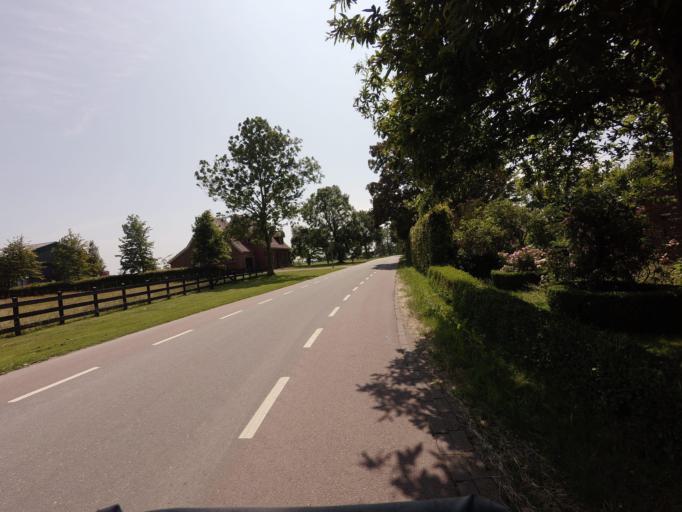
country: NL
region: North Holland
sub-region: Gemeente Opmeer
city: Opmeer
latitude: 52.6822
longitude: 4.9481
